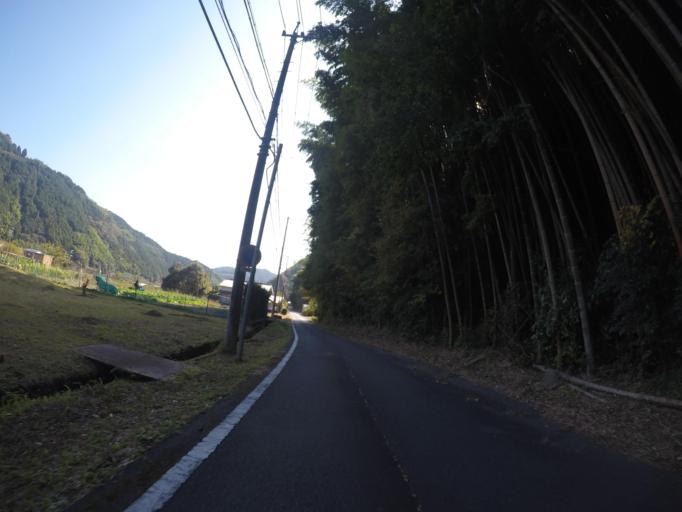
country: JP
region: Shizuoka
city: Shizuoka-shi
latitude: 35.1150
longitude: 138.4583
